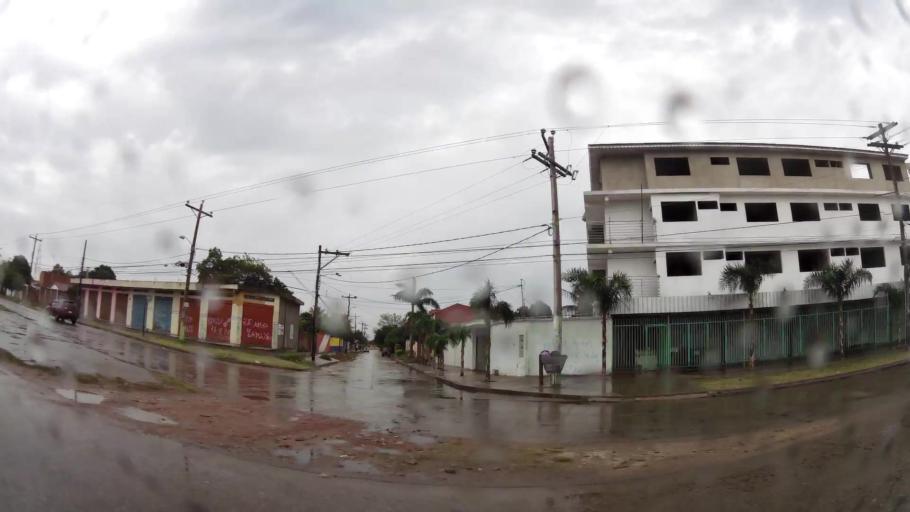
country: BO
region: Santa Cruz
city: Santa Cruz de la Sierra
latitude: -17.8097
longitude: -63.1495
